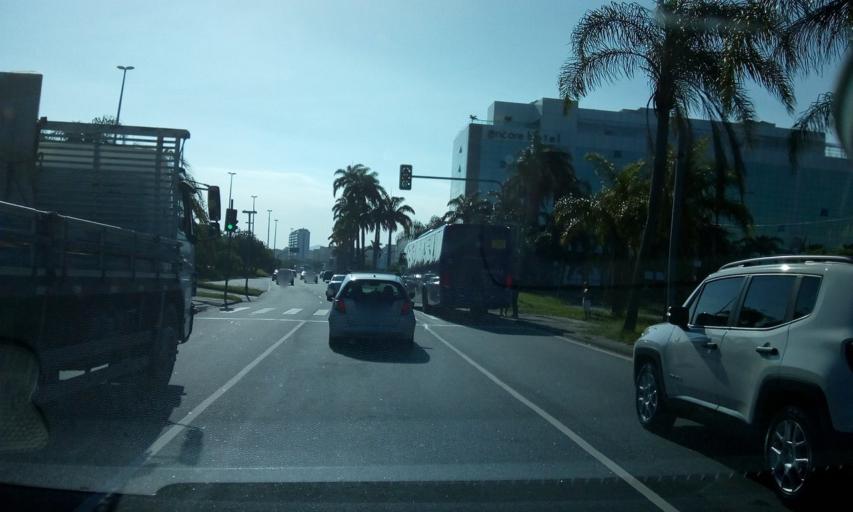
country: BR
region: Rio de Janeiro
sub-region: Nilopolis
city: Nilopolis
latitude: -22.9995
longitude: -43.4076
